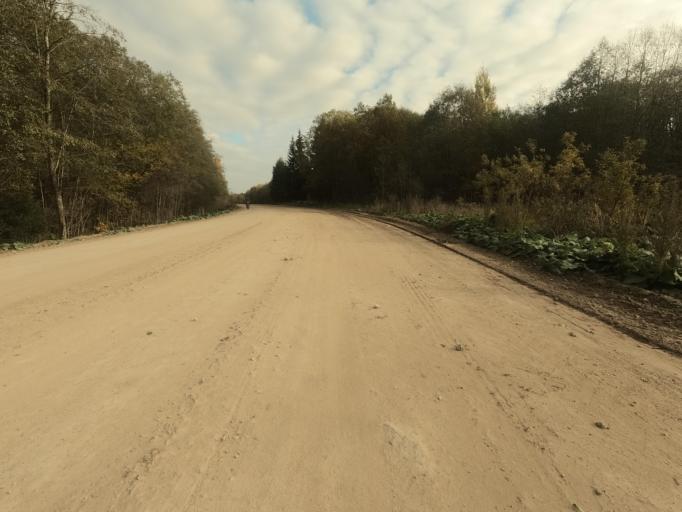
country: RU
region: Novgorod
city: Batetskiy
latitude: 58.7987
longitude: 30.6390
